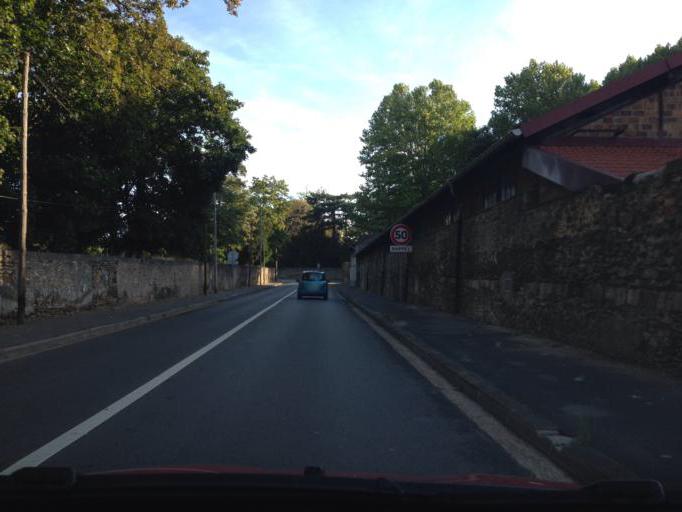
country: FR
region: Ile-de-France
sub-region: Departement des Hauts-de-Seine
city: Meudon
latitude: 48.8001
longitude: 2.2338
